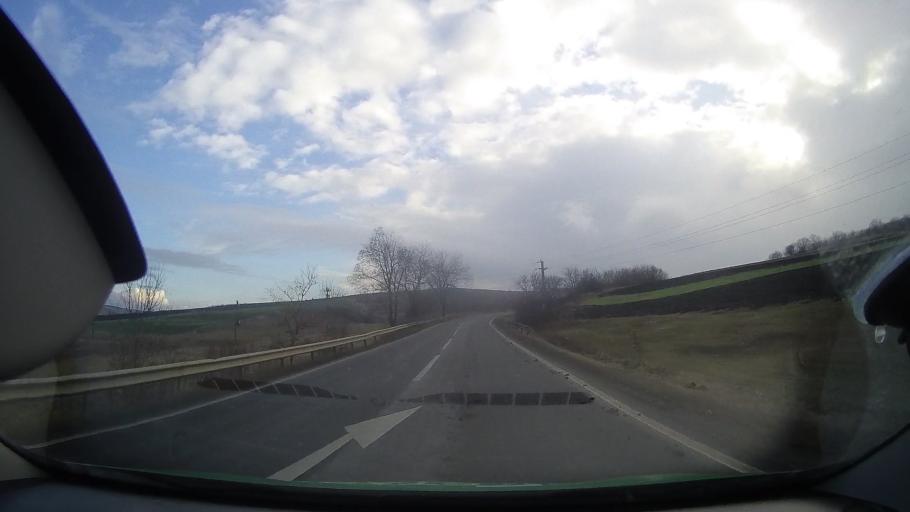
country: RO
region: Mures
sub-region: Comuna Cucerdea
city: Cucerdea
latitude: 46.3628
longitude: 24.2705
